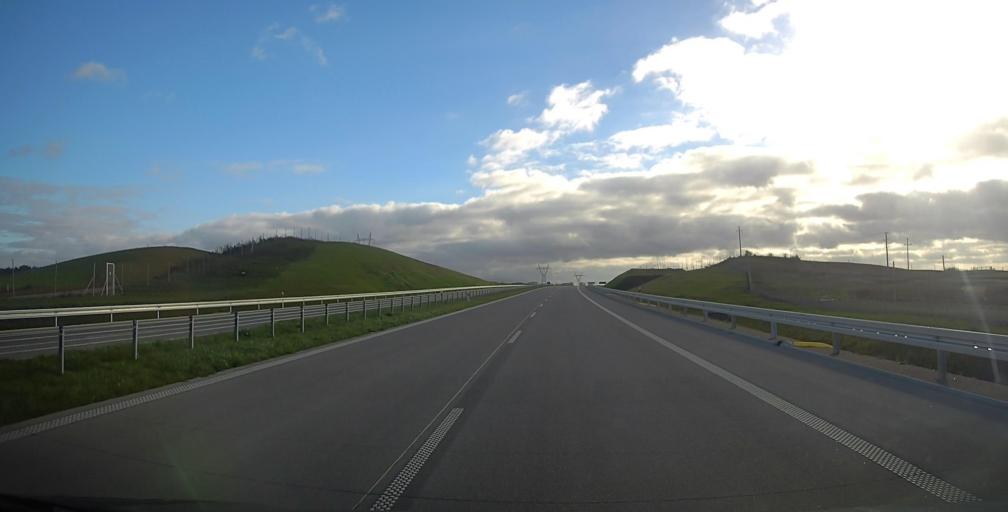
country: PL
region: Podlasie
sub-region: Powiat grajewski
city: Szczuczyn
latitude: 53.6866
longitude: 22.2945
